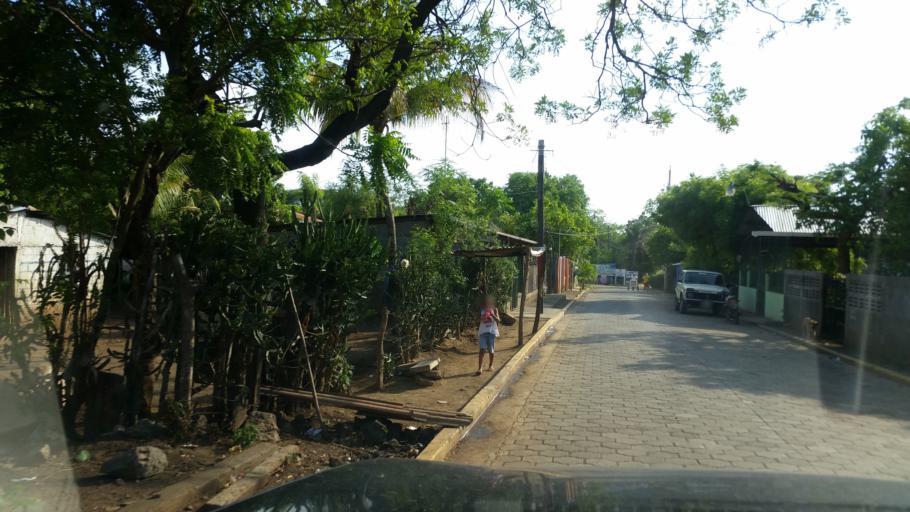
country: NI
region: Managua
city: Masachapa
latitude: 11.7810
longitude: -86.5159
